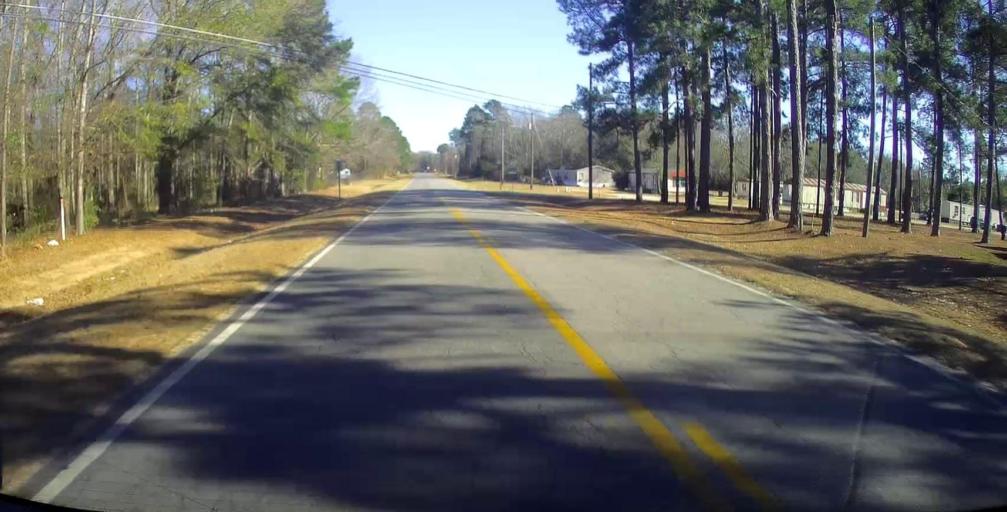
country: US
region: Georgia
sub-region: Taylor County
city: Butler
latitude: 32.5613
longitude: -84.2507
